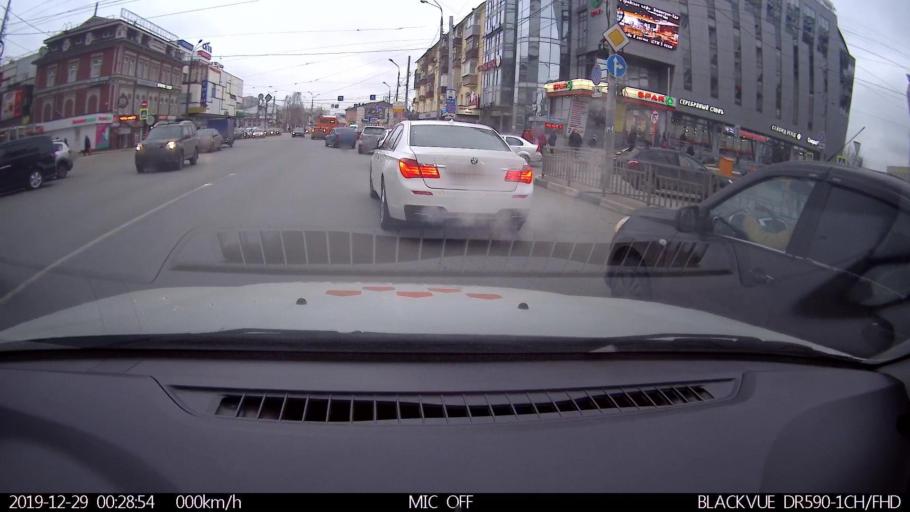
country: RU
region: Nizjnij Novgorod
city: Nizhniy Novgorod
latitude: 56.3201
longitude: 43.9454
